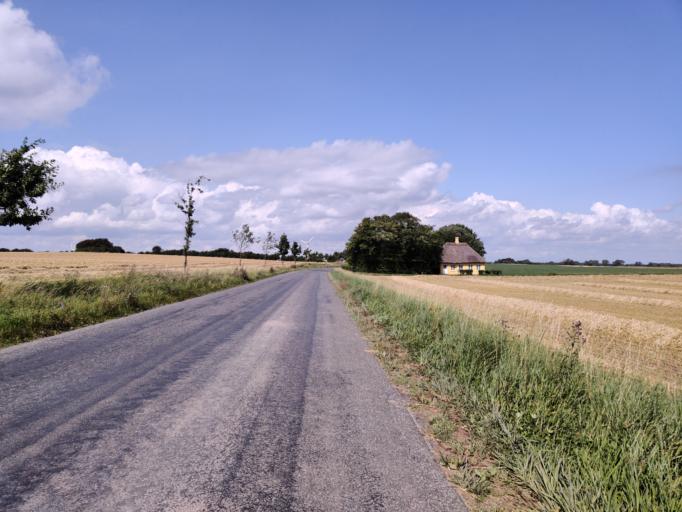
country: DK
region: Zealand
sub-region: Guldborgsund Kommune
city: Nykobing Falster
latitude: 54.6530
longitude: 11.8876
